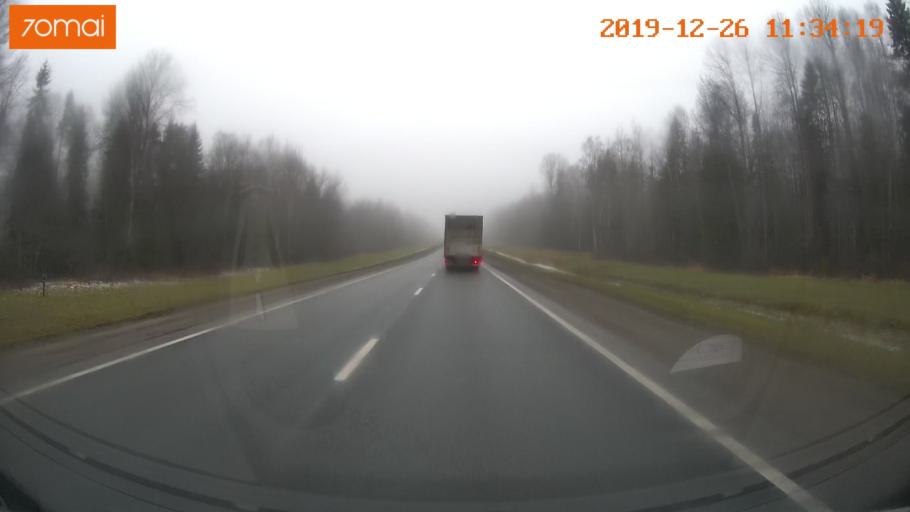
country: RU
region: Vologda
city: Chebsara
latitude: 59.1830
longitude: 38.6906
